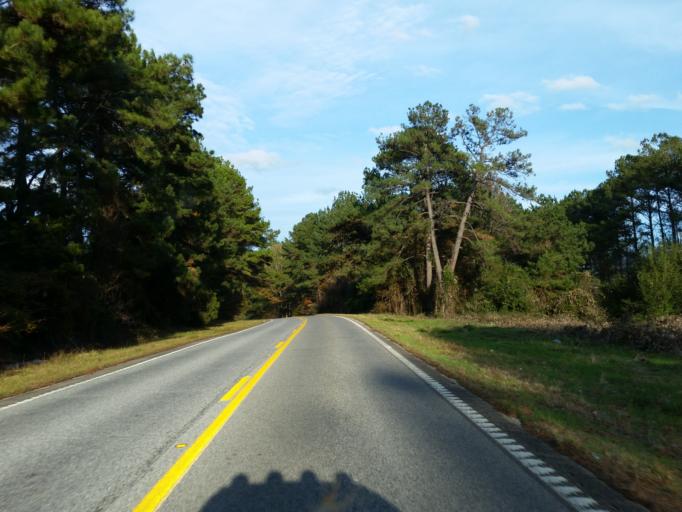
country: US
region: Mississippi
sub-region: Clarke County
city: Stonewall
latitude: 32.1999
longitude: -88.8000
